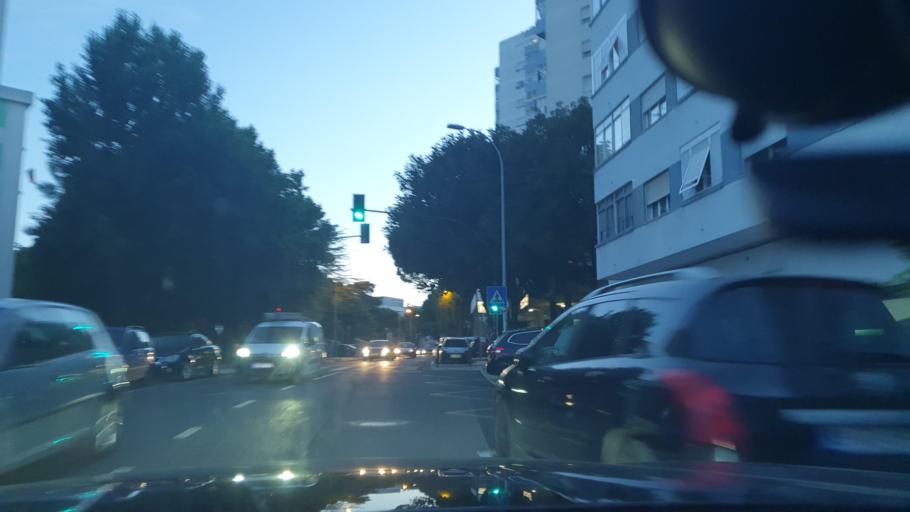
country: PT
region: Lisbon
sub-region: Sintra
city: Queluz
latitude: 38.7614
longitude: -9.2594
